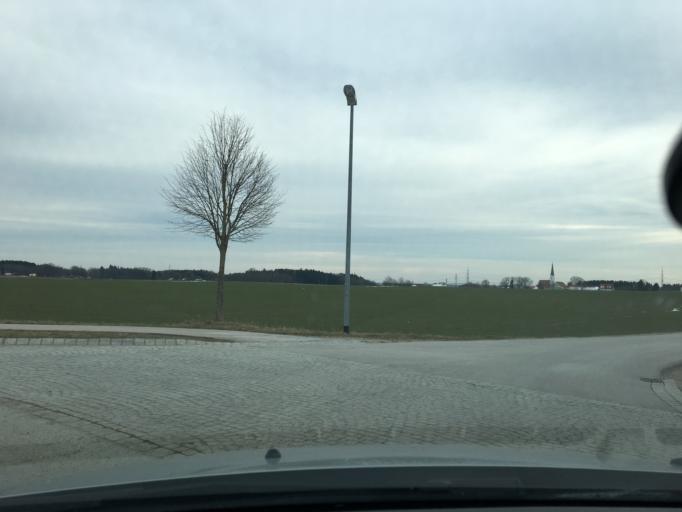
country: DE
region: Bavaria
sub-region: Upper Bavaria
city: Haimhausen
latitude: 48.3102
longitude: 11.5598
